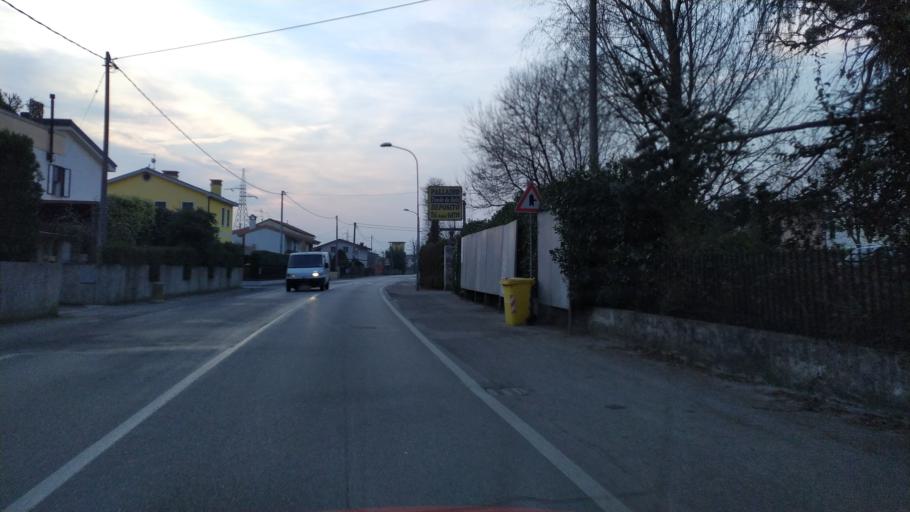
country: IT
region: Veneto
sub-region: Provincia di Vicenza
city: Monticello Conte Otto
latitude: 45.6086
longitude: 11.5745
